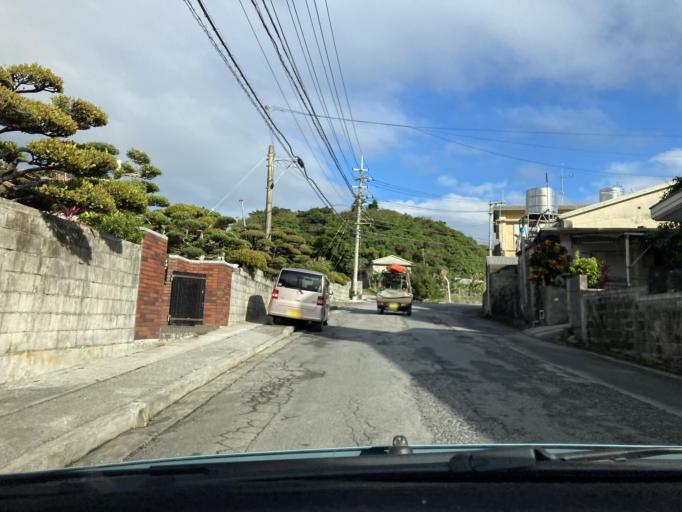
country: JP
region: Okinawa
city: Itoman
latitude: 26.1164
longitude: 127.6733
